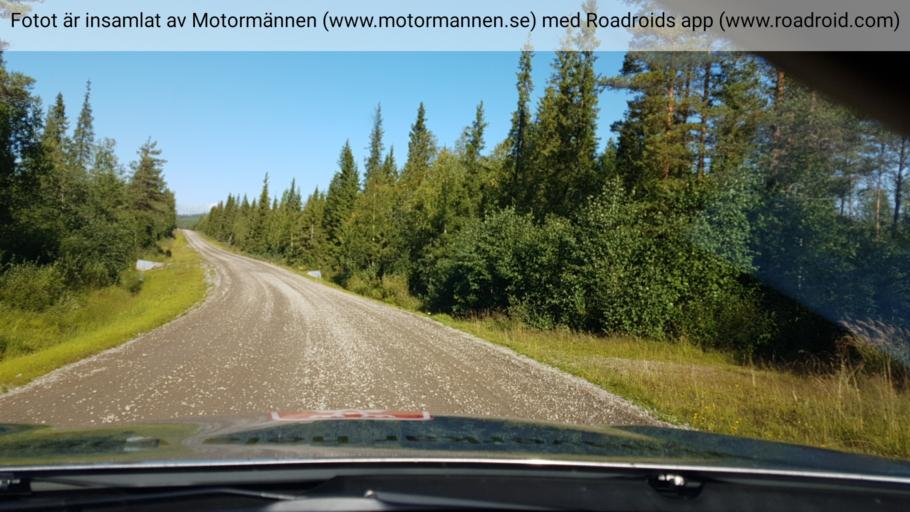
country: SE
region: Norrbotten
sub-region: Overkalix Kommun
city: OEverkalix
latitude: 66.2343
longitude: 23.1606
